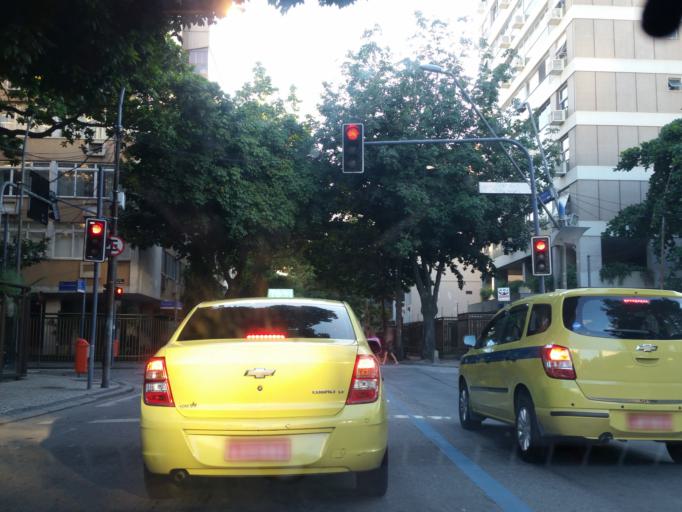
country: BR
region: Rio de Janeiro
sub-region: Rio De Janeiro
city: Rio de Janeiro
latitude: -22.9856
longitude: -43.2235
